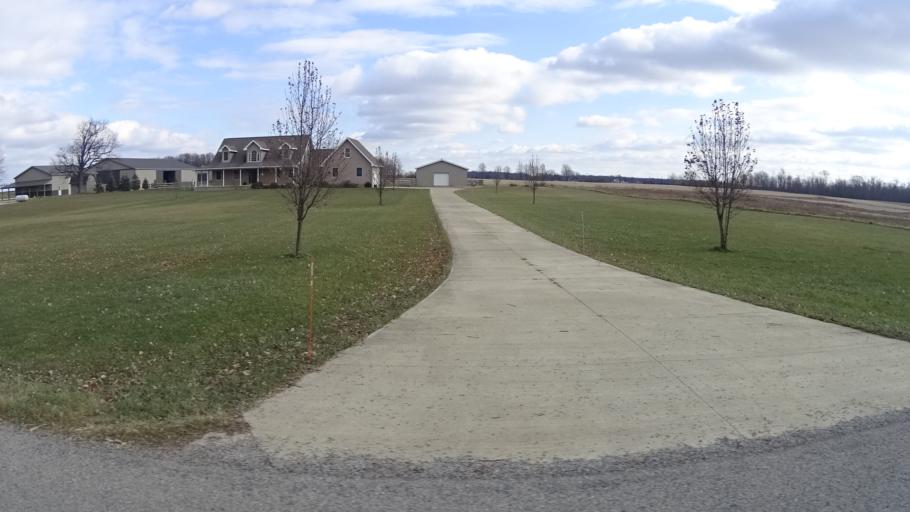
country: US
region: Ohio
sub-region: Lorain County
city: Camden
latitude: 41.2199
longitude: -82.2899
